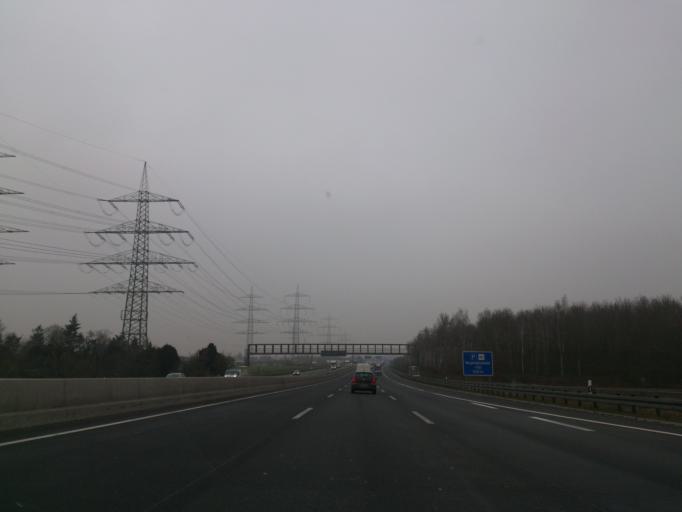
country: DE
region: North Rhine-Westphalia
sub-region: Regierungsbezirk Dusseldorf
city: Neuss
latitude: 51.1998
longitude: 6.6532
